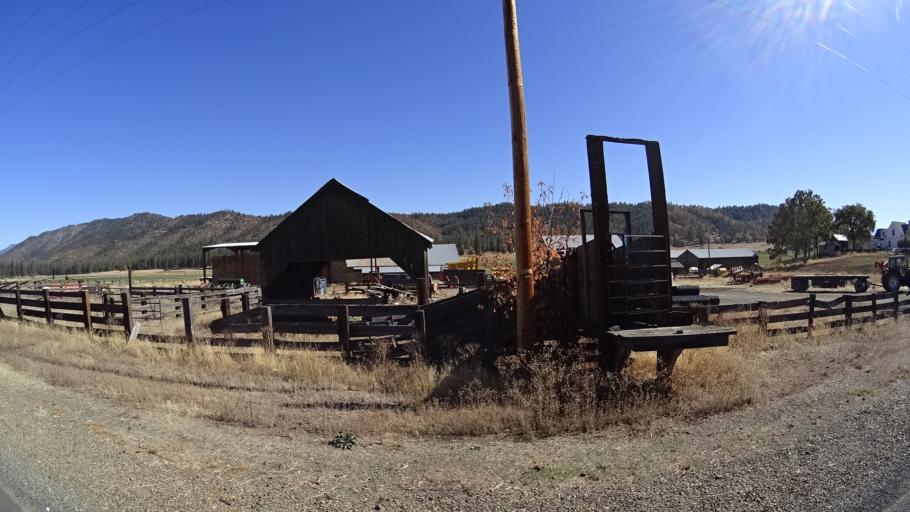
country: US
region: California
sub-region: Siskiyou County
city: Yreka
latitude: 41.5735
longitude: -122.9216
